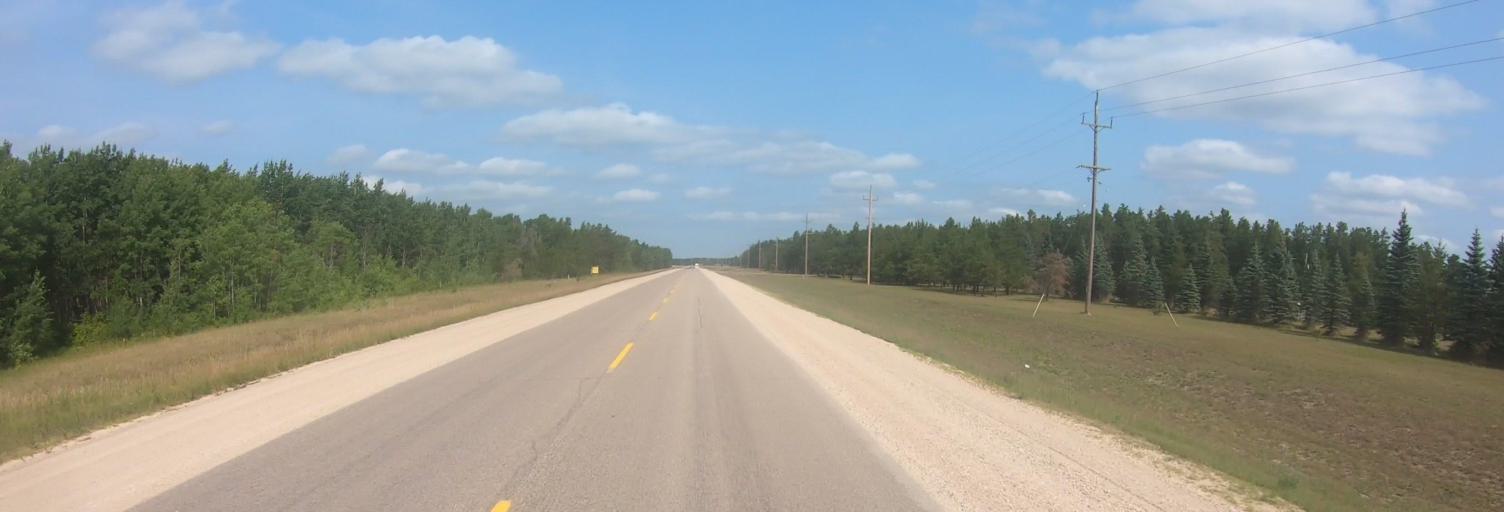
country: CA
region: Manitoba
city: La Broquerie
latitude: 49.2537
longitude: -96.3558
